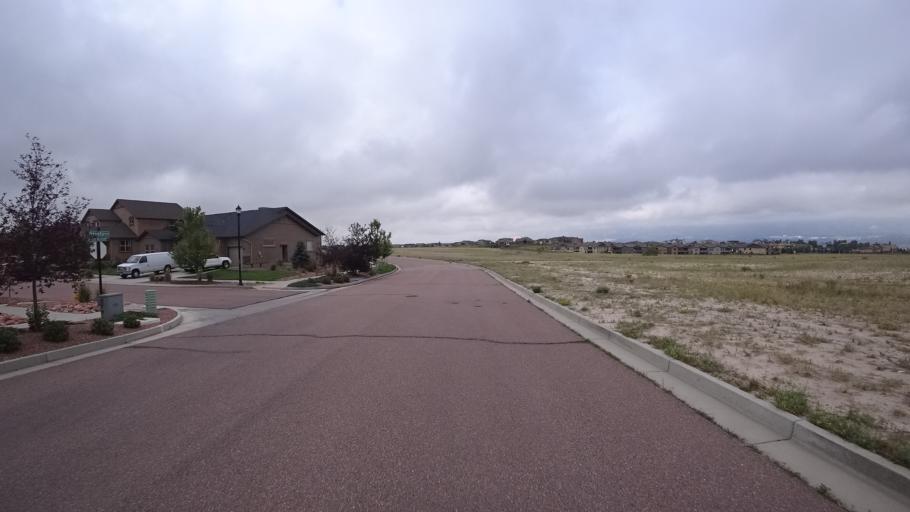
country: US
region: Colorado
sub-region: El Paso County
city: Gleneagle
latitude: 39.0176
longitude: -104.7836
